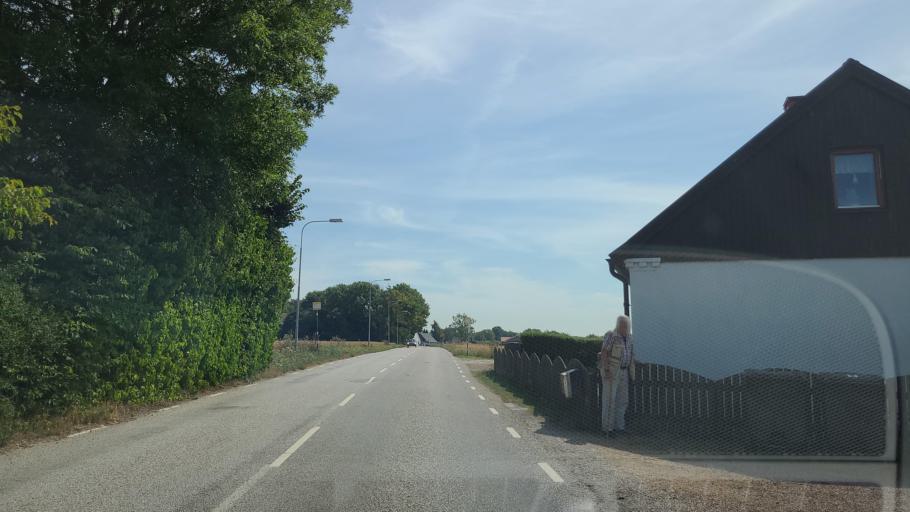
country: SE
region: Skane
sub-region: Trelleborgs Kommun
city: Trelleborg
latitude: 55.3929
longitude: 13.1256
